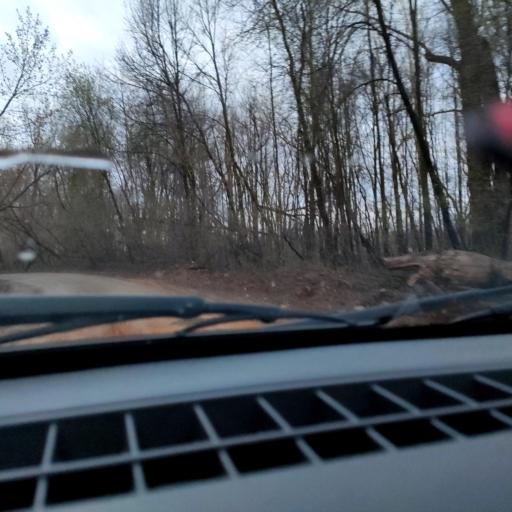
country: RU
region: Bashkortostan
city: Ufa
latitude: 54.6732
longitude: 55.9551
